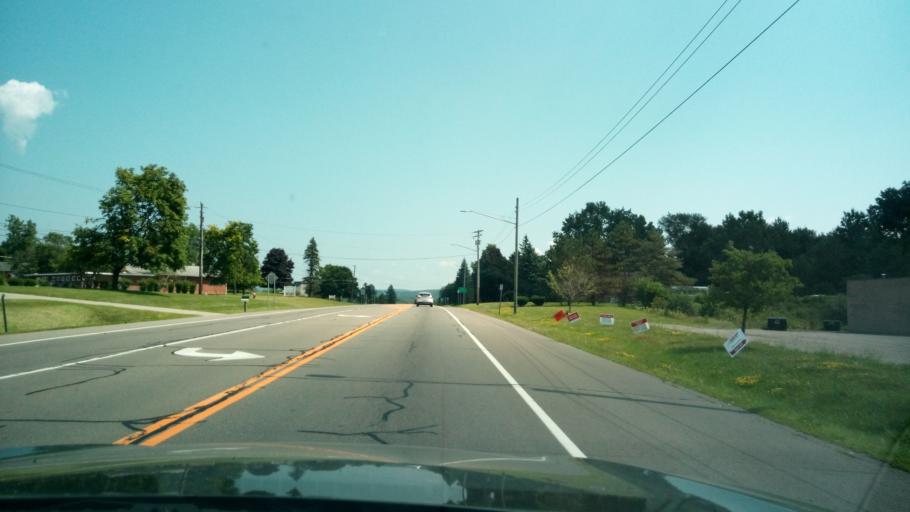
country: US
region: New York
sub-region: Chemung County
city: Horseheads
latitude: 42.1769
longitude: -76.8371
